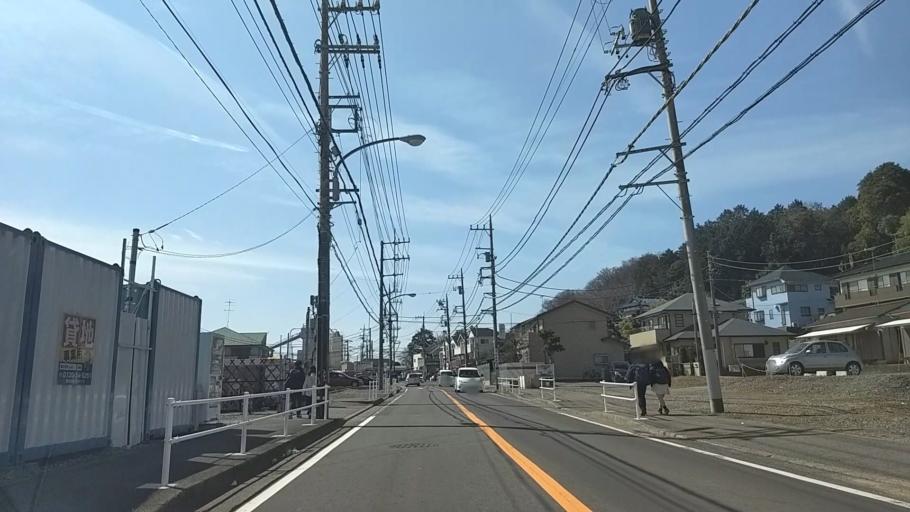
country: JP
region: Kanagawa
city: Fujisawa
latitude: 35.3826
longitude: 139.4978
